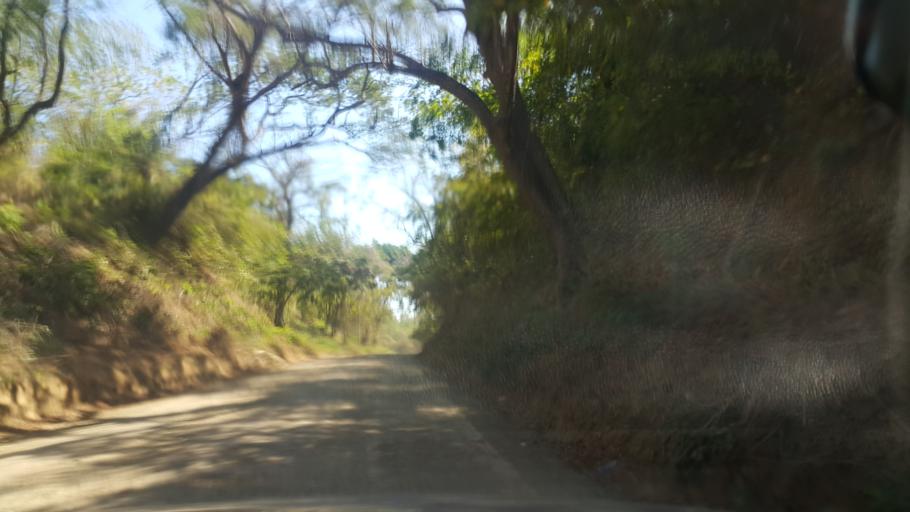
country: NI
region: Rivas
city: San Juan del Sur
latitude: 11.2805
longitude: -85.8890
